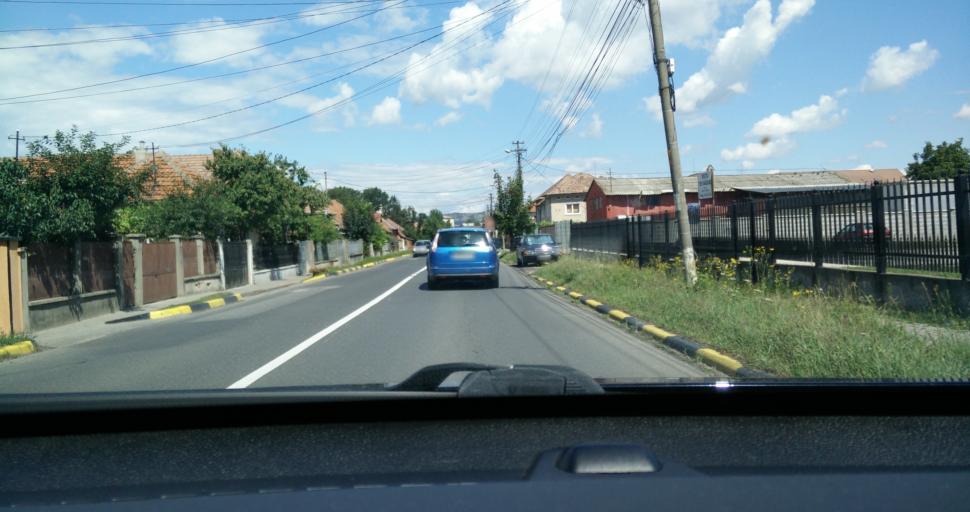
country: RO
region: Alba
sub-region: Municipiul Sebes
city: Sebes
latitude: 45.9464
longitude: 23.5645
